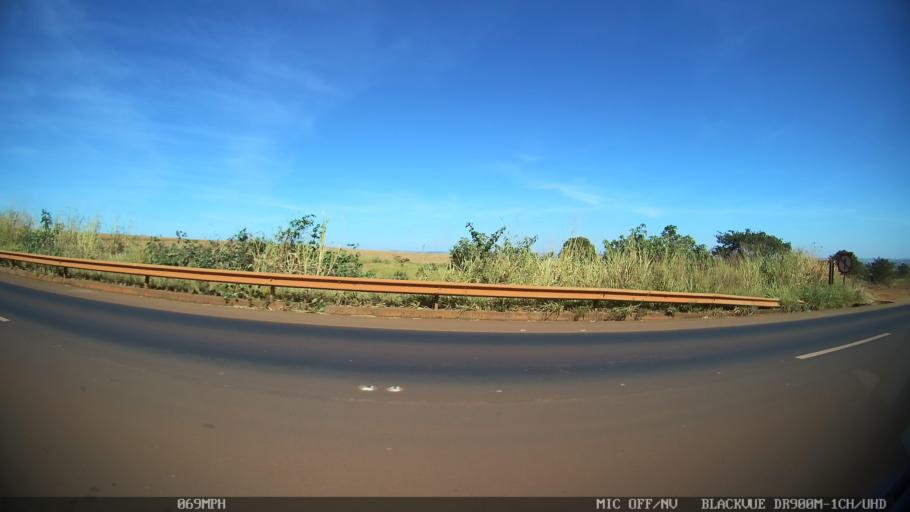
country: BR
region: Sao Paulo
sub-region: Sao Joaquim Da Barra
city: Sao Joaquim da Barra
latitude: -20.5507
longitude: -47.7443
